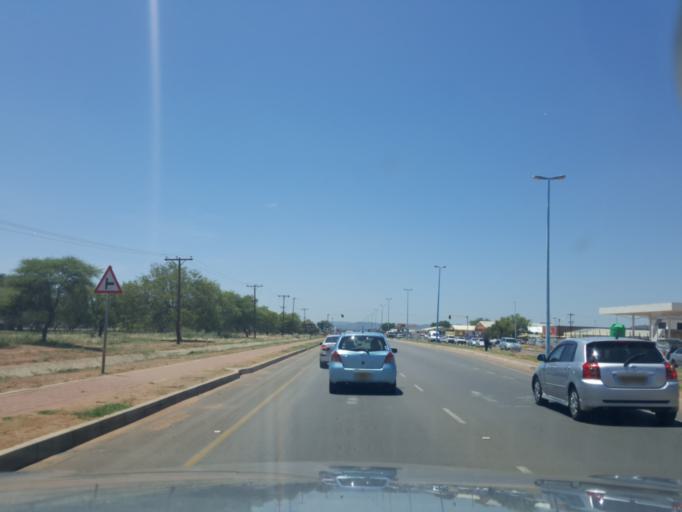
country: BW
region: Kweneng
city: Mogoditshane
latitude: -24.6107
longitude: 25.8603
